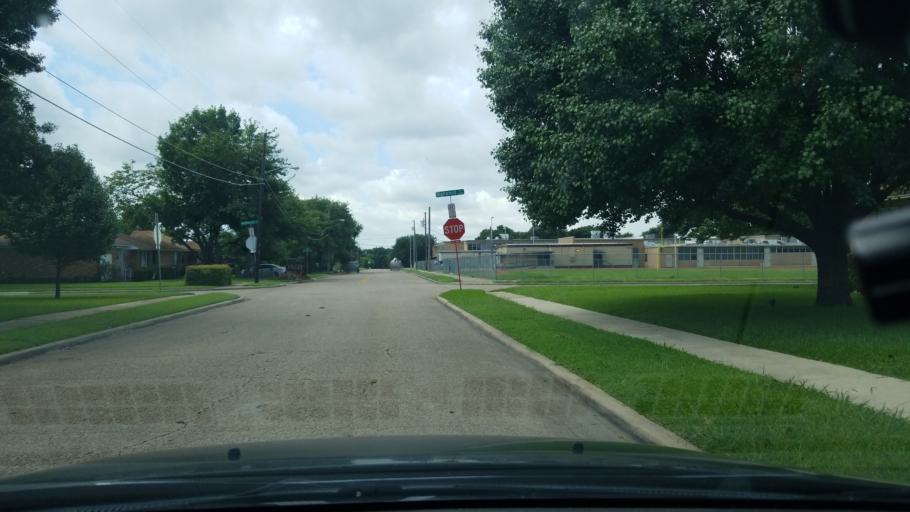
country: US
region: Texas
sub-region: Dallas County
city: Garland
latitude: 32.8292
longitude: -96.6789
